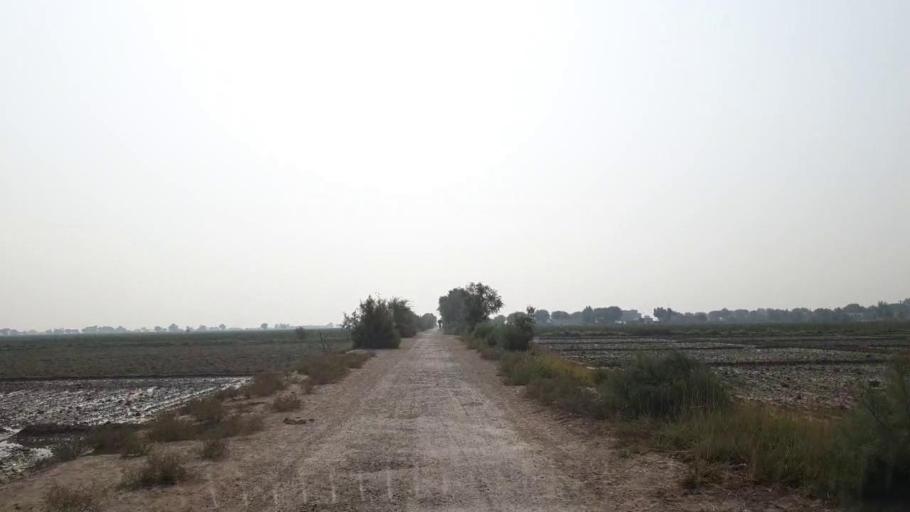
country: PK
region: Sindh
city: Bhan
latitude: 26.4688
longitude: 67.7389
